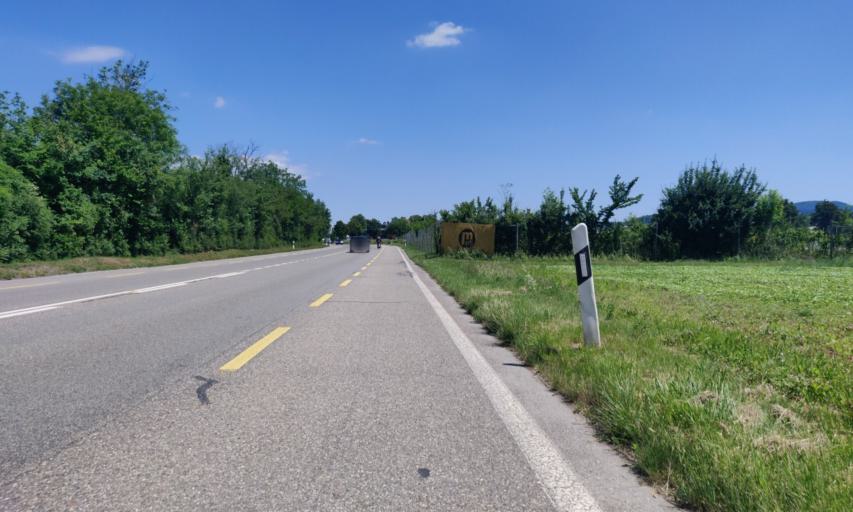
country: CH
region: Basel-Landschaft
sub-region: Bezirk Liestal
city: Pratteln
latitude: 47.5313
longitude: 7.6942
